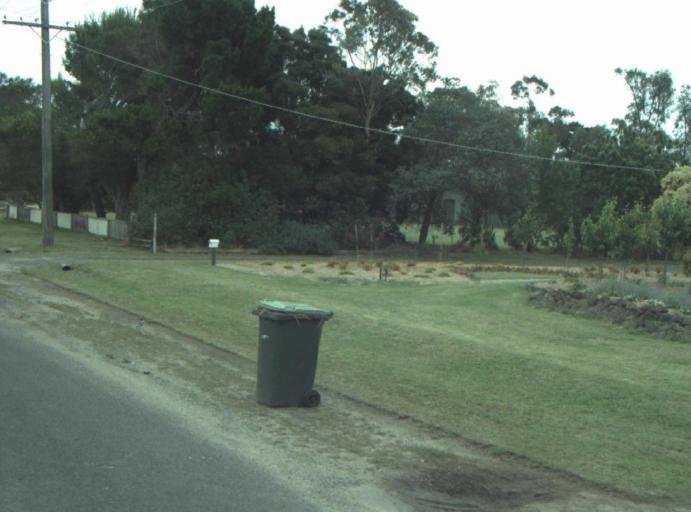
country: AU
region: Victoria
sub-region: Greater Geelong
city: East Geelong
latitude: -38.1697
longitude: 144.4079
